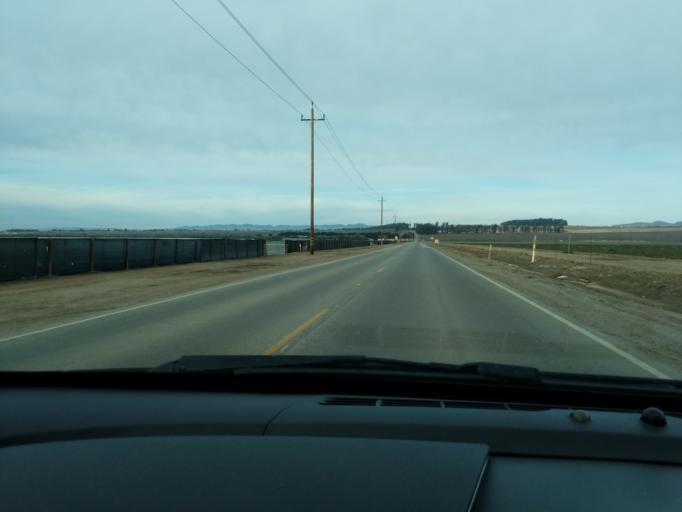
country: US
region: California
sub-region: Santa Barbara County
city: Guadalupe
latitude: 35.0069
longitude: -120.5692
